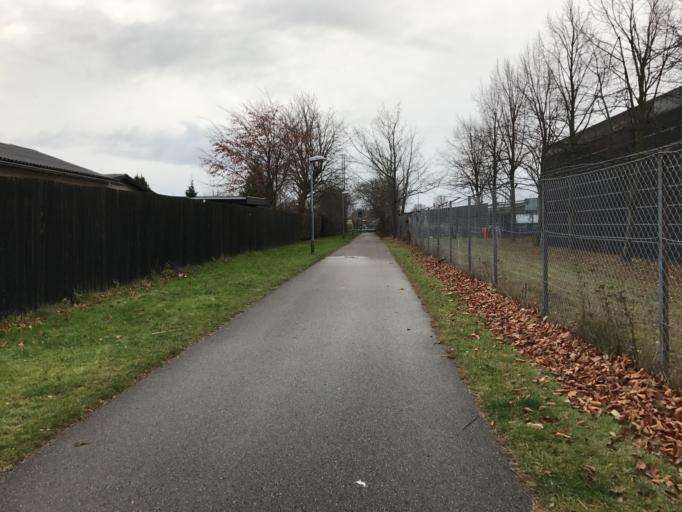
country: DK
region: Capital Region
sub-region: Hoje-Taastrup Kommune
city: Taastrup
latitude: 55.6594
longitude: 12.2974
